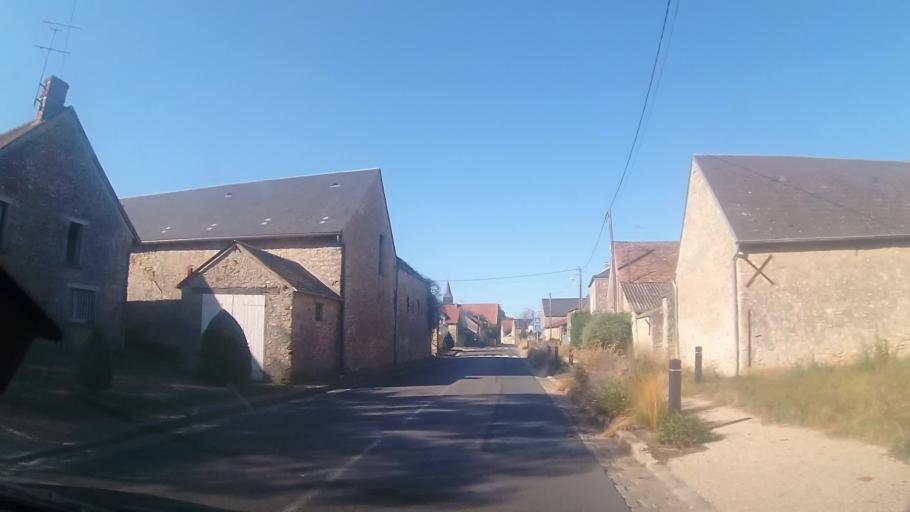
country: FR
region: Ile-de-France
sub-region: Departement de l'Essonne
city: Corbreuse
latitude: 48.4674
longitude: 1.9311
